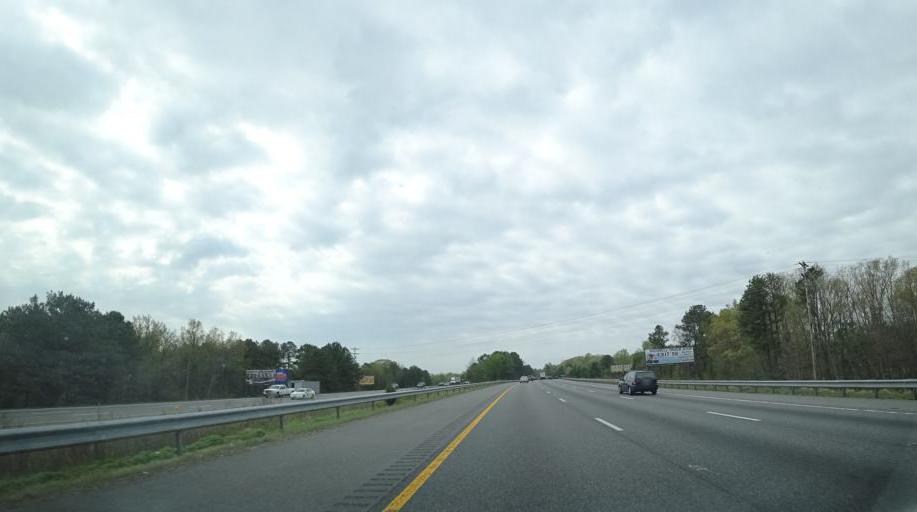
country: US
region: Virginia
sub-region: Hanover County
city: Ashland
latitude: 37.8601
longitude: -77.4540
